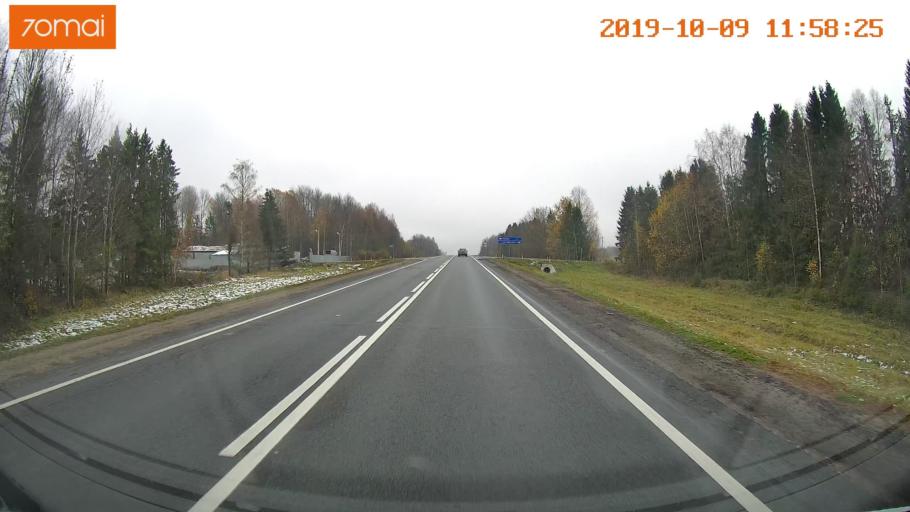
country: RU
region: Vologda
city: Gryazovets
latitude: 58.7184
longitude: 40.2964
